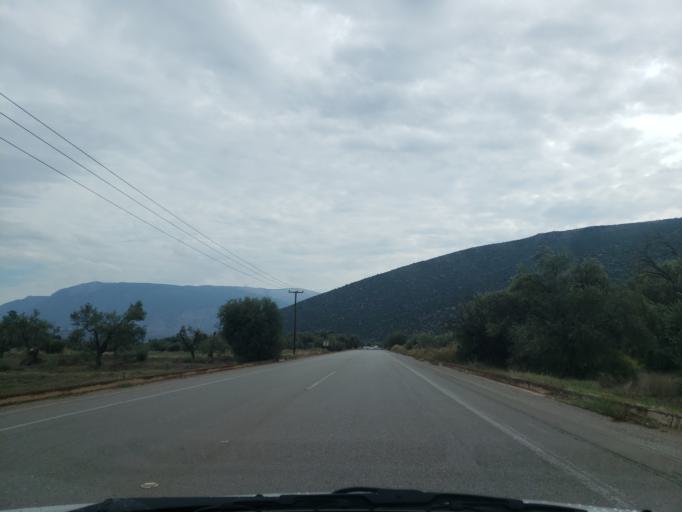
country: GR
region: Central Greece
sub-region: Nomos Fokidos
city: Itea
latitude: 38.4880
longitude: 22.4189
